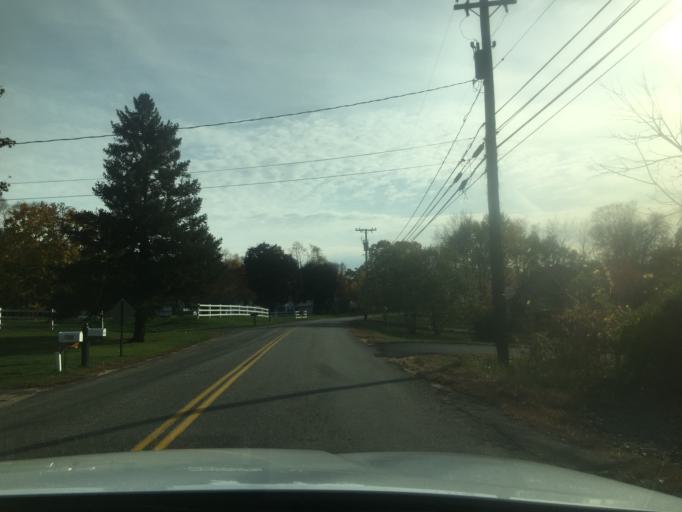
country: US
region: Connecticut
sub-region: Hartford County
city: Broad Brook
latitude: 41.8893
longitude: -72.5690
